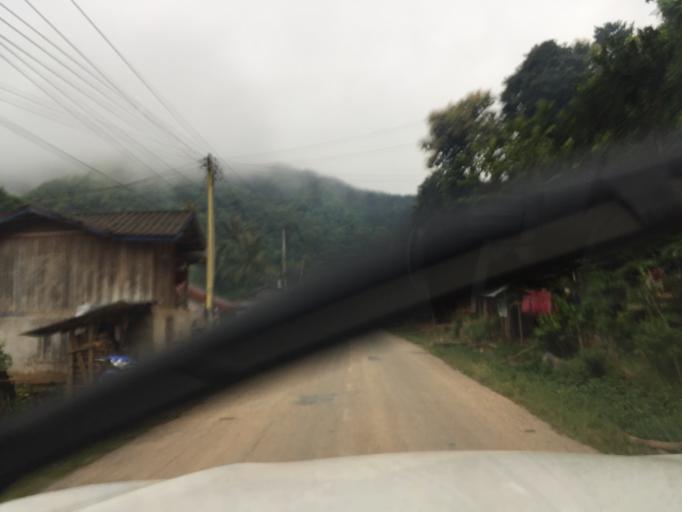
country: LA
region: Phongsali
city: Khoa
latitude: 21.0701
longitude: 102.3770
